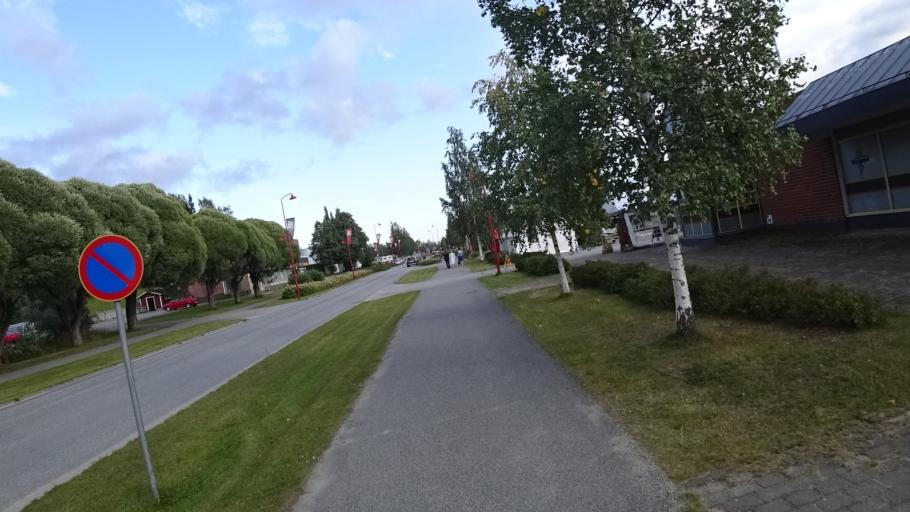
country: FI
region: North Karelia
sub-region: Joensuu
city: Ilomantsi
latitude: 62.6730
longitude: 30.9301
